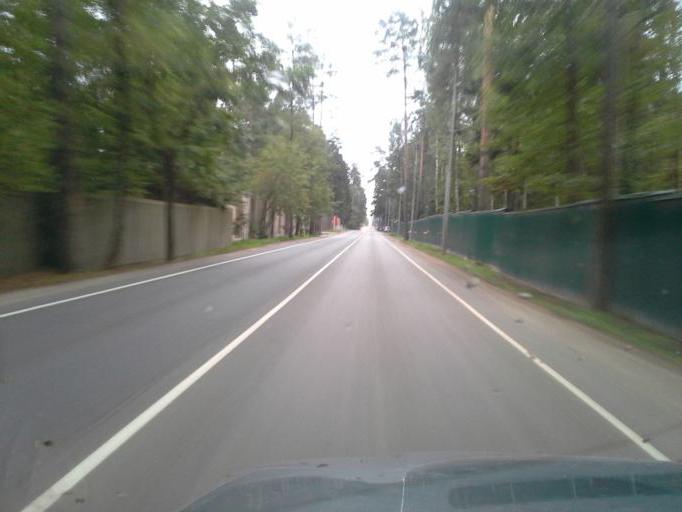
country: RU
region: Moskovskaya
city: Nazar'yevo
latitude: 55.7021
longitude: 37.0624
